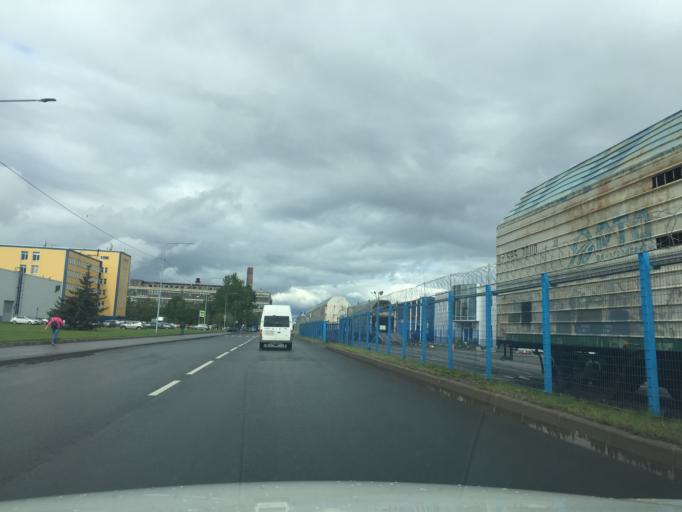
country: RU
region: St.-Petersburg
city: Sosnovaya Polyana
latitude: 59.8529
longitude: 30.1252
